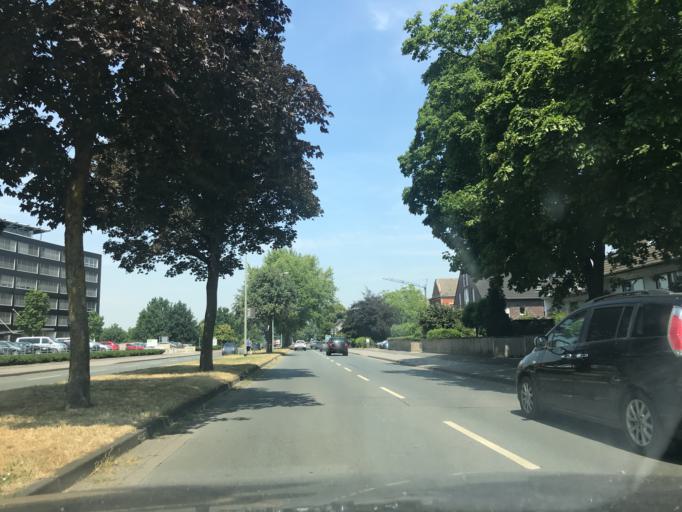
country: DE
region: North Rhine-Westphalia
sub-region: Regierungsbezirk Dusseldorf
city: Wesel
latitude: 51.6657
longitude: 6.6096
